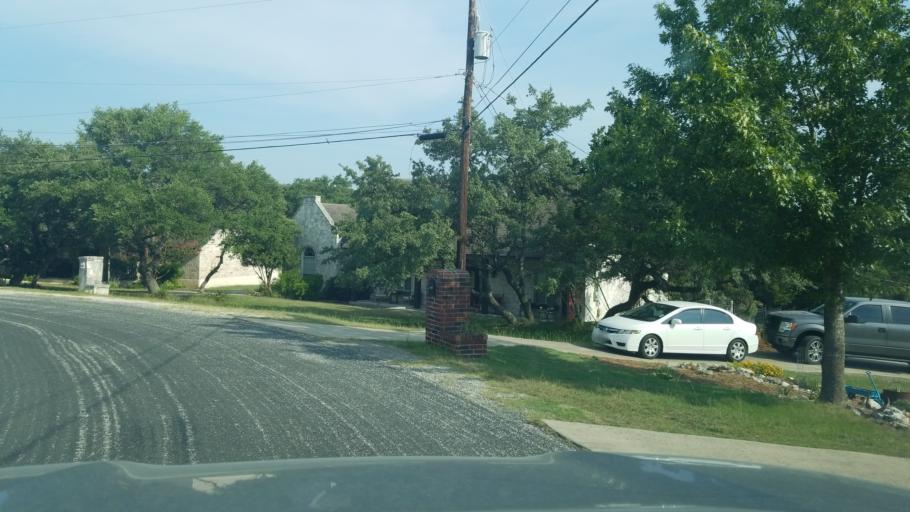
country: US
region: Texas
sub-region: Bexar County
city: Timberwood Park
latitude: 29.7026
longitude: -98.4941
